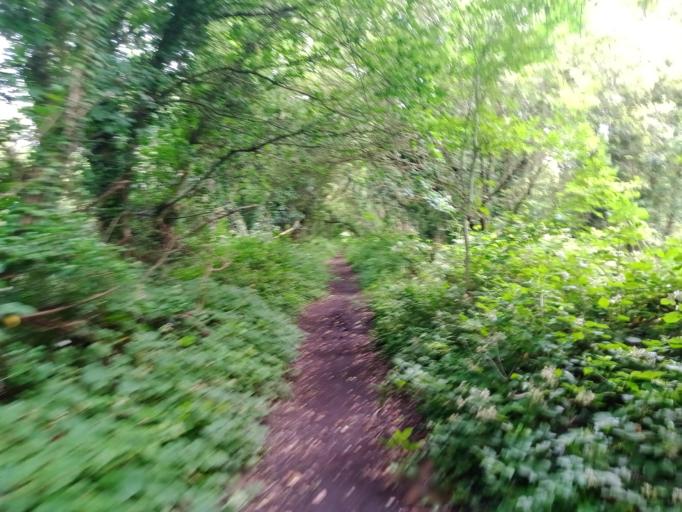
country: IE
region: Leinster
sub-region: Laois
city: Abbeyleix
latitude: 52.8817
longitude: -7.3506
